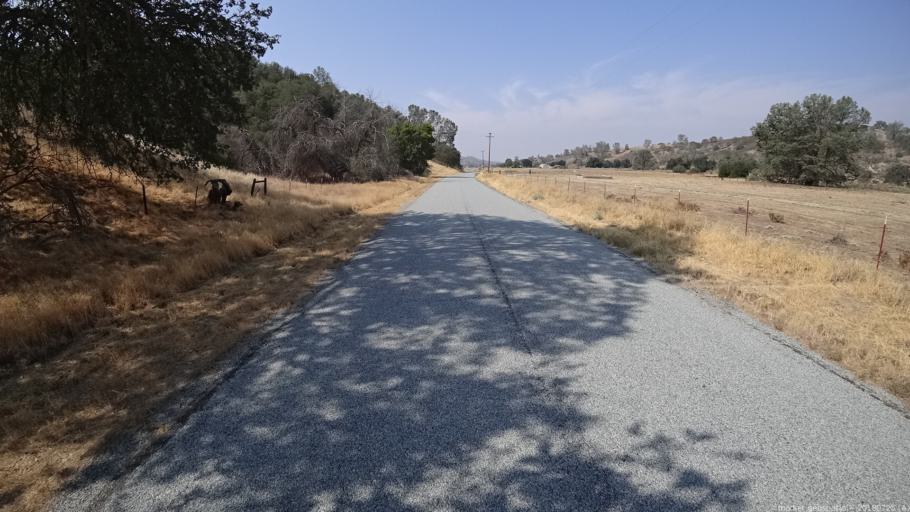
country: US
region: California
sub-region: San Luis Obispo County
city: San Miguel
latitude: 35.8544
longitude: -120.6051
